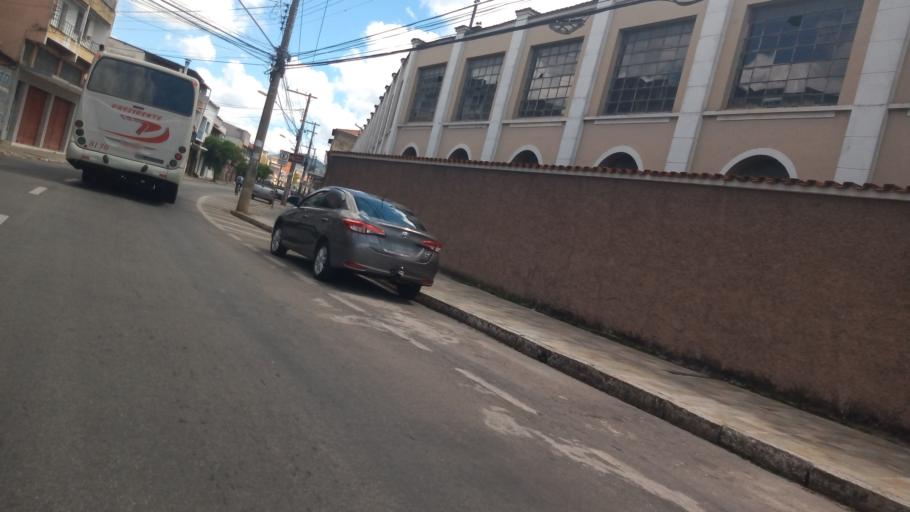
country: BR
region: Minas Gerais
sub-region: Sao Joao Del Rei
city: Sao Joao del Rei
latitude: -21.1301
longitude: -44.2511
